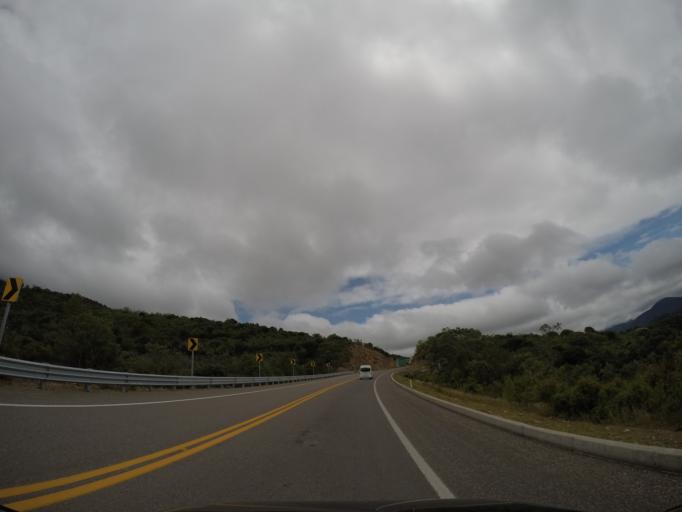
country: MX
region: Oaxaca
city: San Lorenzo Albarradas
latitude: 16.9256
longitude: -96.2587
